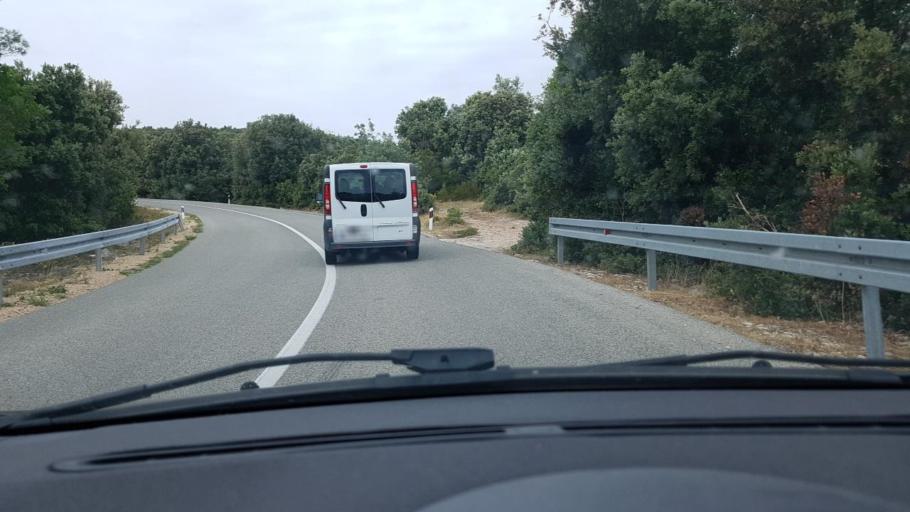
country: HR
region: Dubrovacko-Neretvanska
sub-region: Grad Korcula
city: Zrnovo
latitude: 42.9436
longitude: 17.0074
